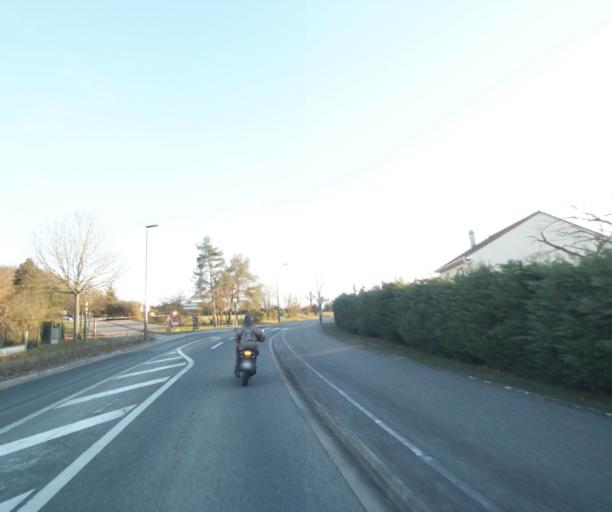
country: FR
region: Lorraine
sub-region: Departement de Meurthe-et-Moselle
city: Pulnoy
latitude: 48.6956
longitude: 6.2555
